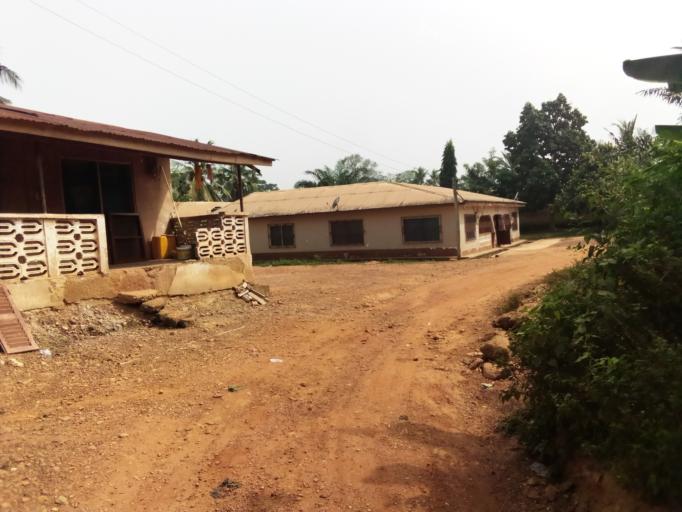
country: CI
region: Sud-Comoe
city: Ayame
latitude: 5.8277
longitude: -2.8189
